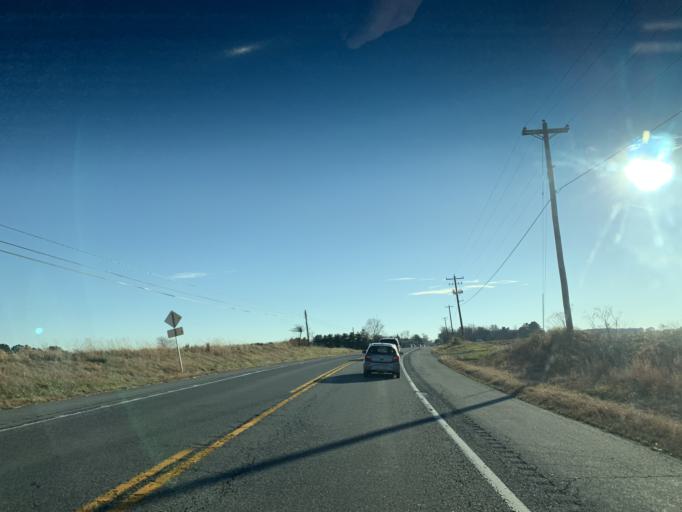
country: US
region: Delaware
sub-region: New Castle County
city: Middletown
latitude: 39.4162
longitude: -75.8615
